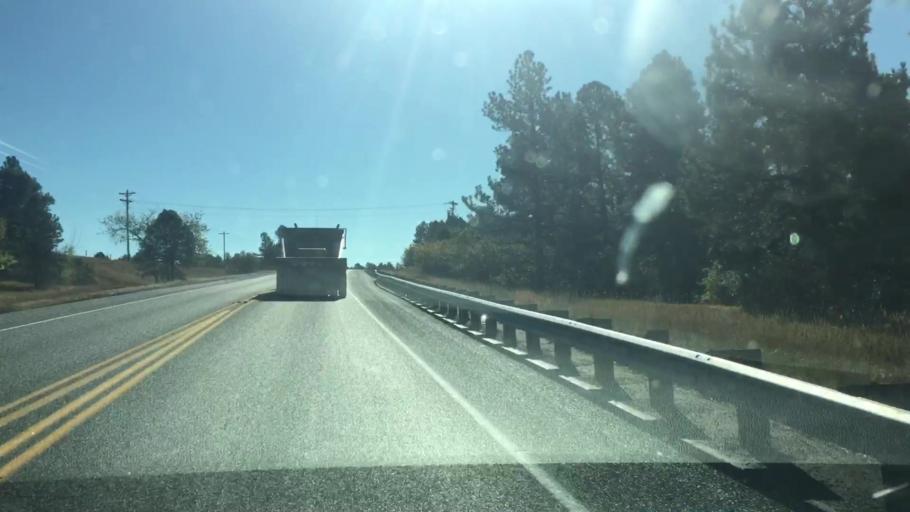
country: US
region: Colorado
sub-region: Elbert County
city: Ponderosa Park
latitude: 39.3759
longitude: -104.6909
